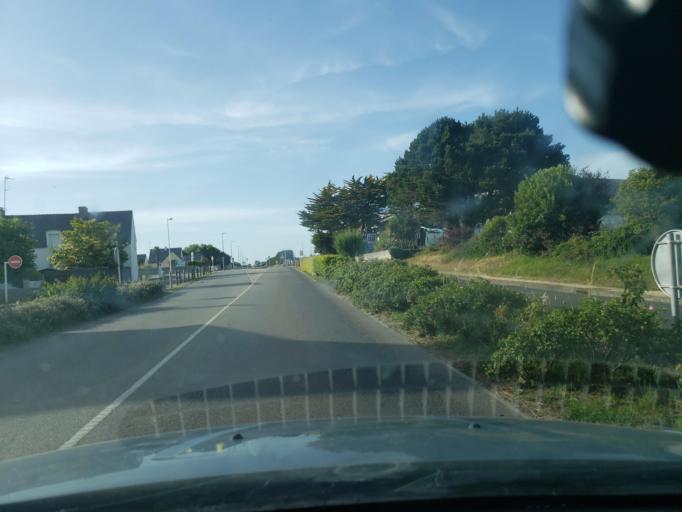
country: FR
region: Brittany
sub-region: Departement du Finistere
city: Guilvinec
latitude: 47.8021
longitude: -4.2776
